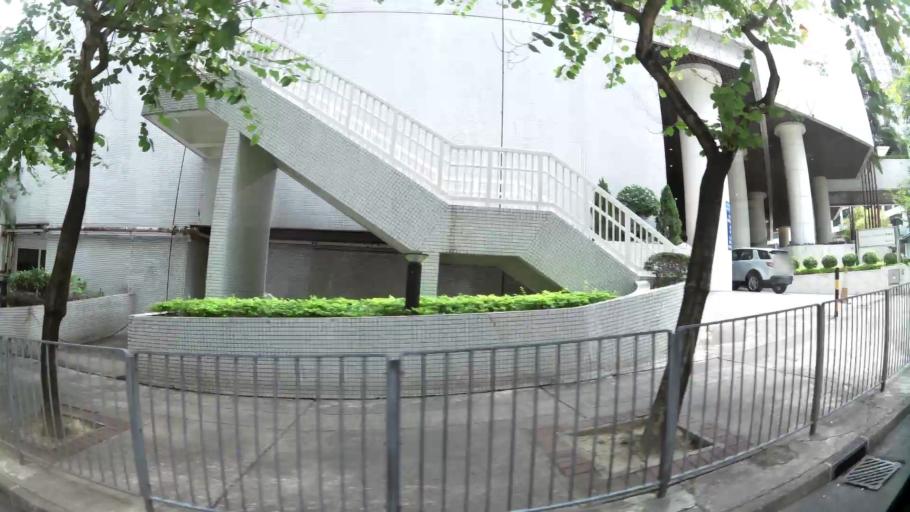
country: HK
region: Wanchai
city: Wan Chai
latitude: 22.2838
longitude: 114.2155
